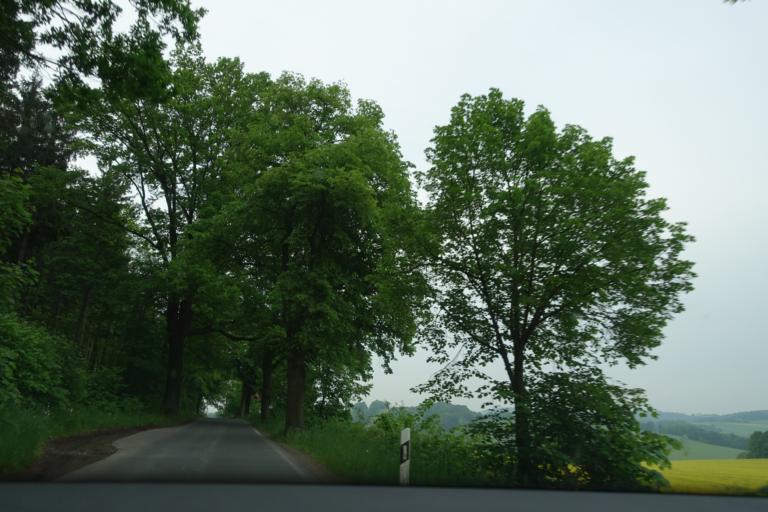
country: DE
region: Saxony
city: Borstendorf
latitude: 50.7805
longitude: 13.1763
